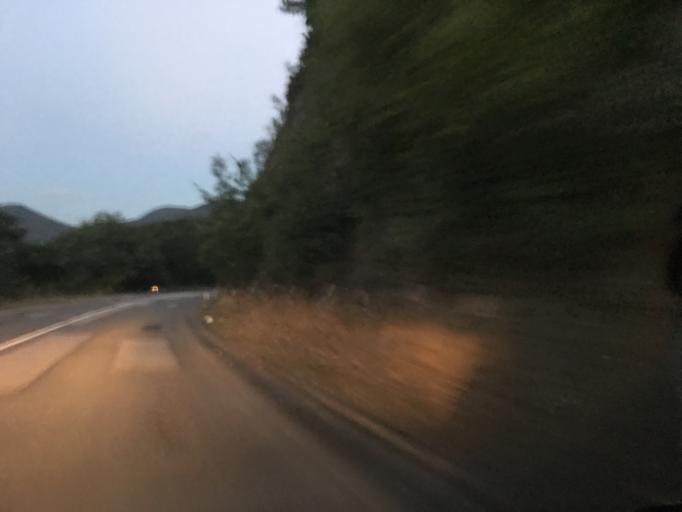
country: RO
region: Caras-Severin
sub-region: Comuna Berzasca
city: Berzasca
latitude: 44.6291
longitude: 21.9878
